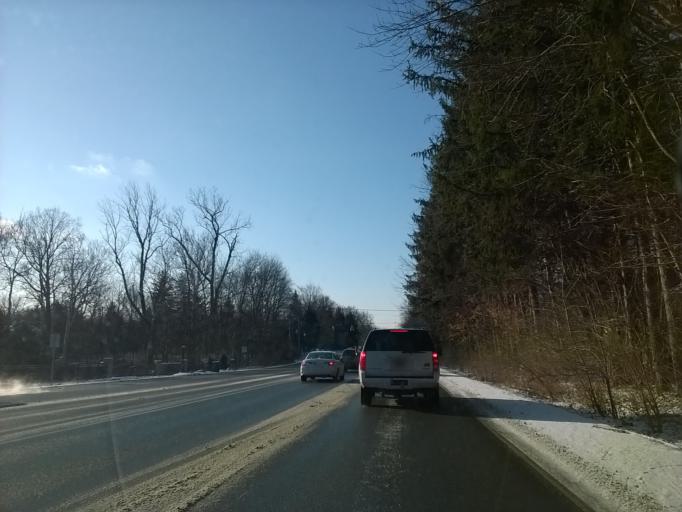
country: US
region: Indiana
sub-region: Marion County
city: Meridian Hills
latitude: 39.8844
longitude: -86.1580
